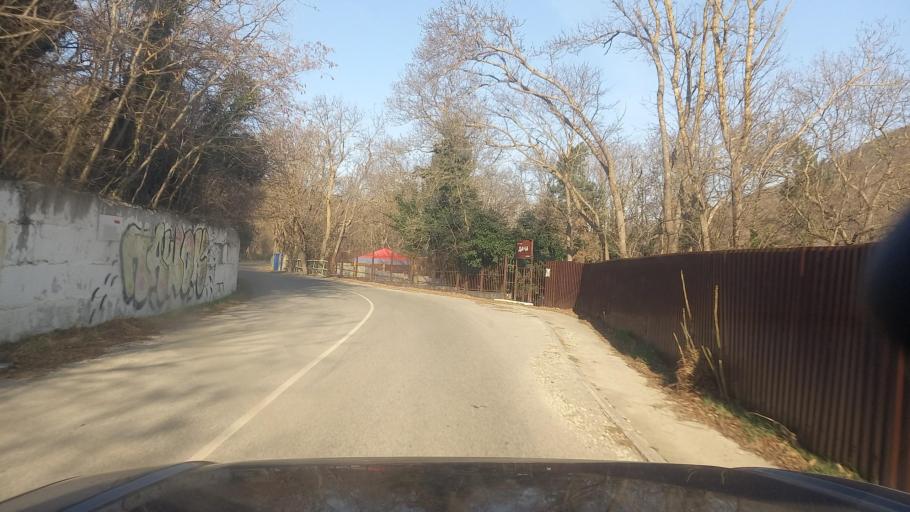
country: RU
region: Krasnodarskiy
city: Myskhako
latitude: 44.6647
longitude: 37.6851
